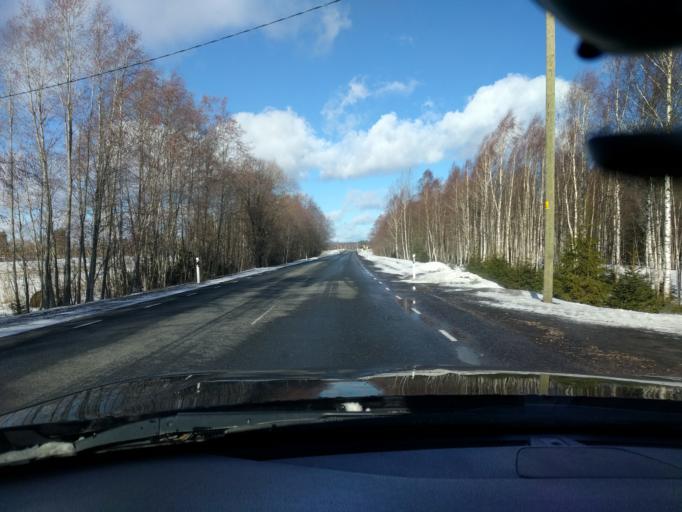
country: EE
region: Harju
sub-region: Anija vald
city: Kehra
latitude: 59.2285
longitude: 25.3920
